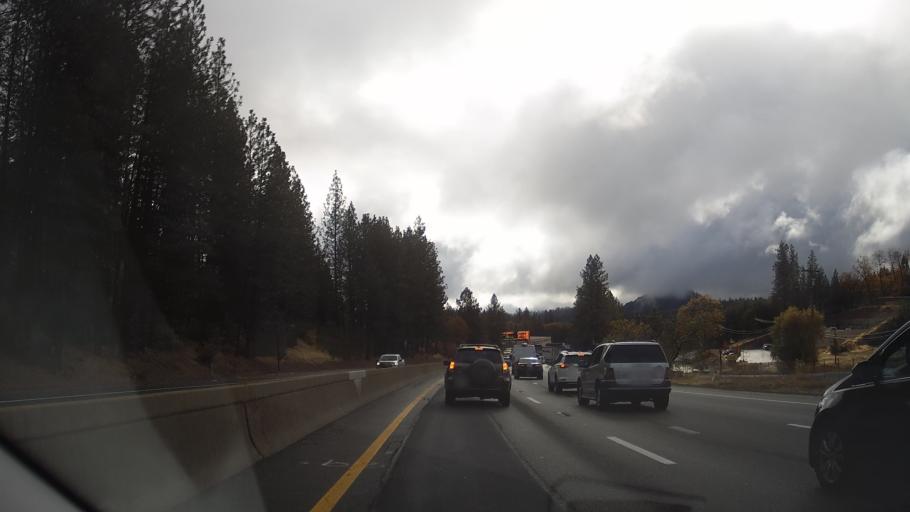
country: US
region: California
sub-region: Placer County
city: Colfax
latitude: 39.0933
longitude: -120.9501
